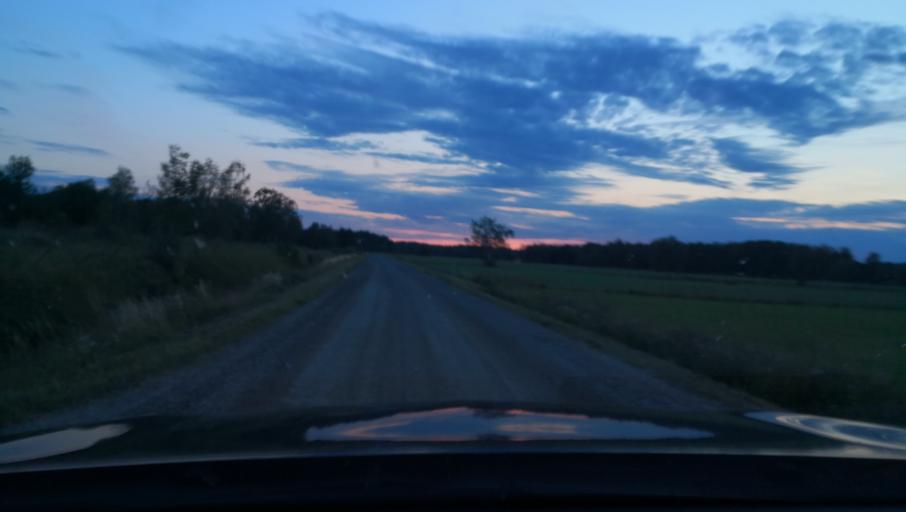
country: SE
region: Uppsala
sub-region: Heby Kommun
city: OEstervala
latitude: 60.0118
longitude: 17.3180
